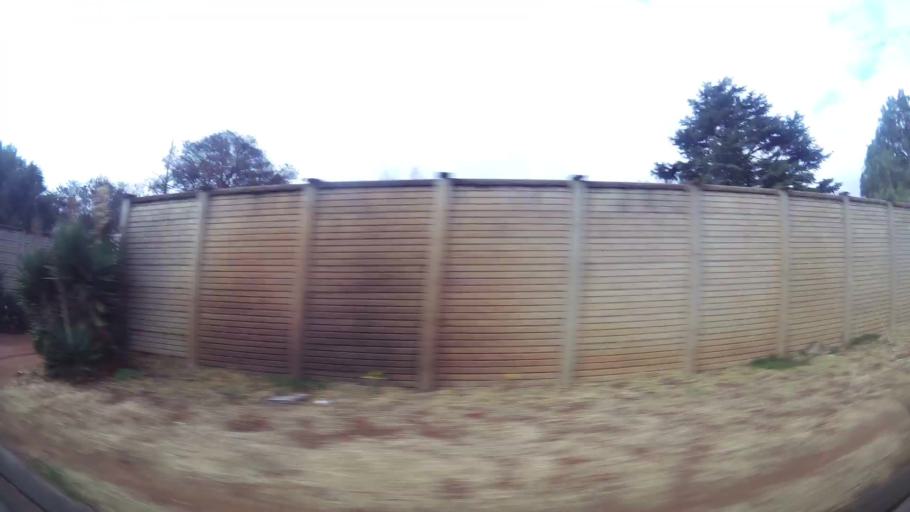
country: ZA
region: Gauteng
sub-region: Sedibeng District Municipality
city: Meyerton
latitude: -26.5927
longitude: 27.9969
